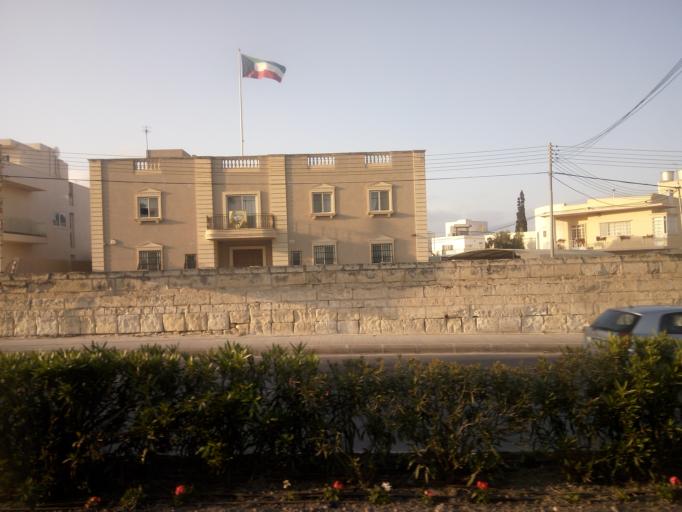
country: MT
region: Balzan
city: Balzan
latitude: 35.8934
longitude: 14.4553
